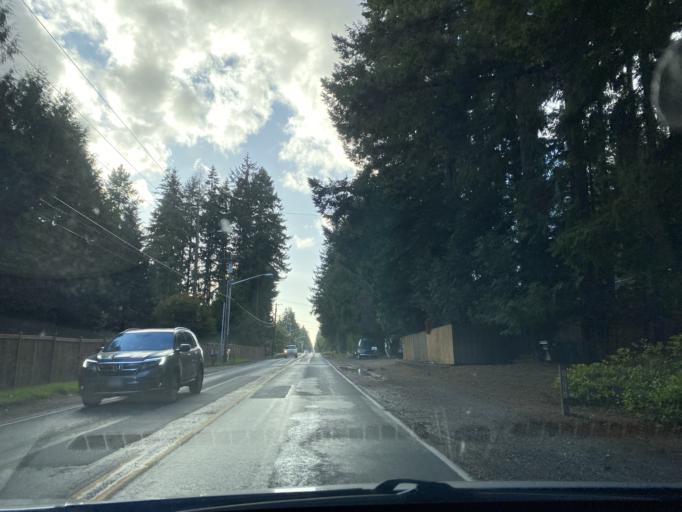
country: US
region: Washington
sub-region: Pierce County
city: South Hill
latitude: 47.1184
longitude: -122.2863
